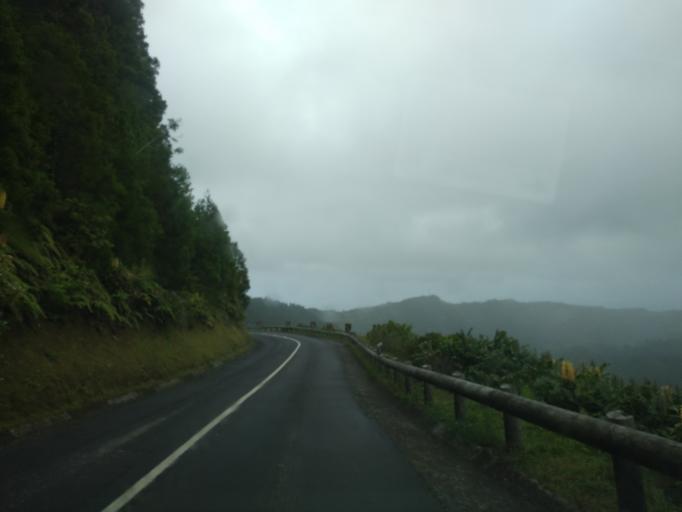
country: PT
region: Azores
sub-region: Ponta Delgada
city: Arrifes
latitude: 37.8390
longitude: -25.7909
